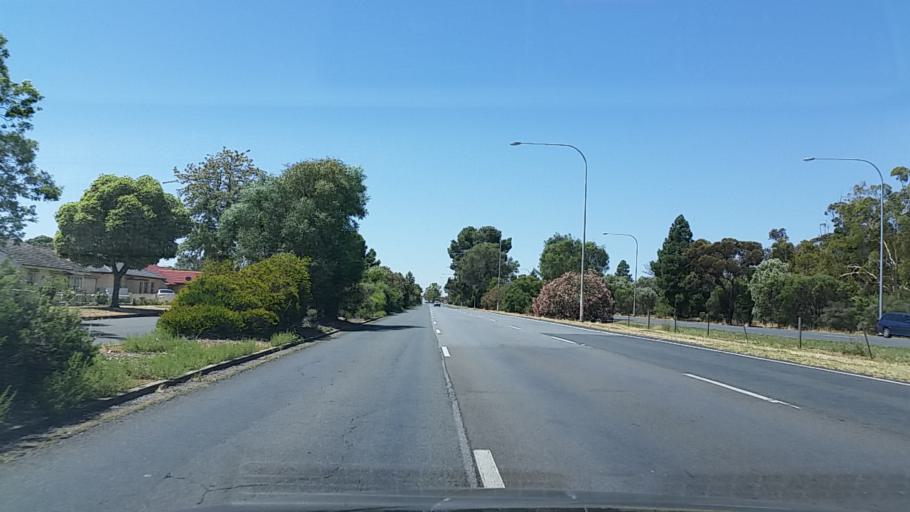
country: AU
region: South Australia
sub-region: Salisbury
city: Elizabeth
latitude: -34.7108
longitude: 138.6762
